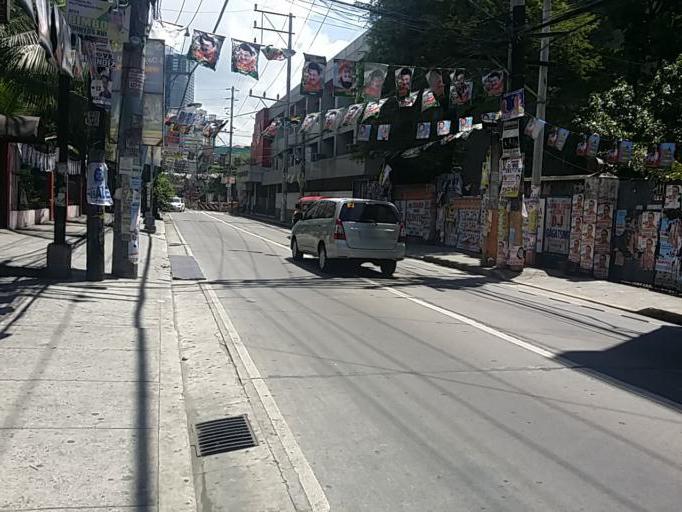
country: PH
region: Metro Manila
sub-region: City of Manila
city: Quiapo
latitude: 14.6025
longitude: 120.9885
